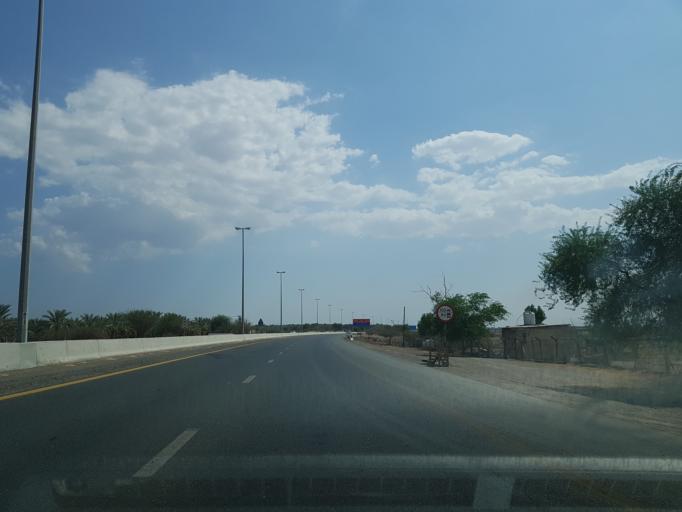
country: AE
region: Ash Shariqah
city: Adh Dhayd
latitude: 25.2407
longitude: 55.9153
